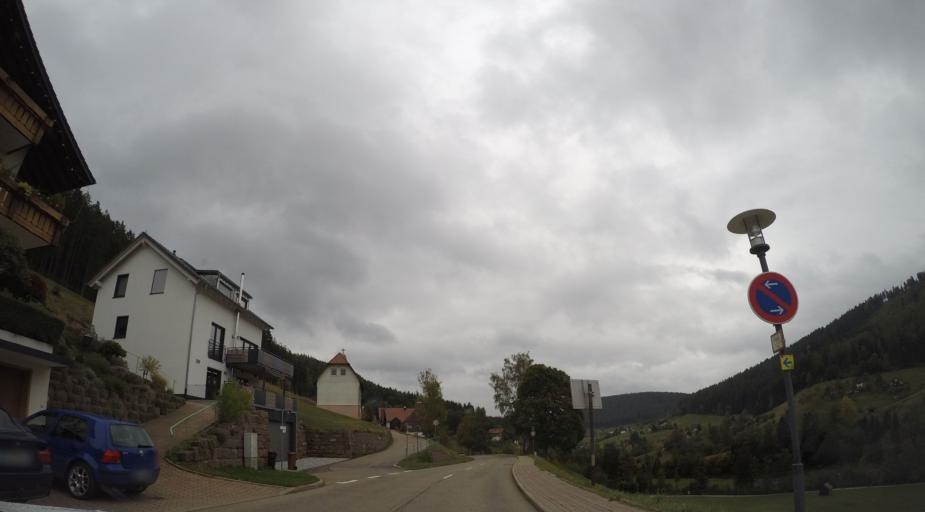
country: DE
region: Baden-Wuerttemberg
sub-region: Karlsruhe Region
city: Baiersbronn
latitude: 48.5358
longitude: 8.3592
